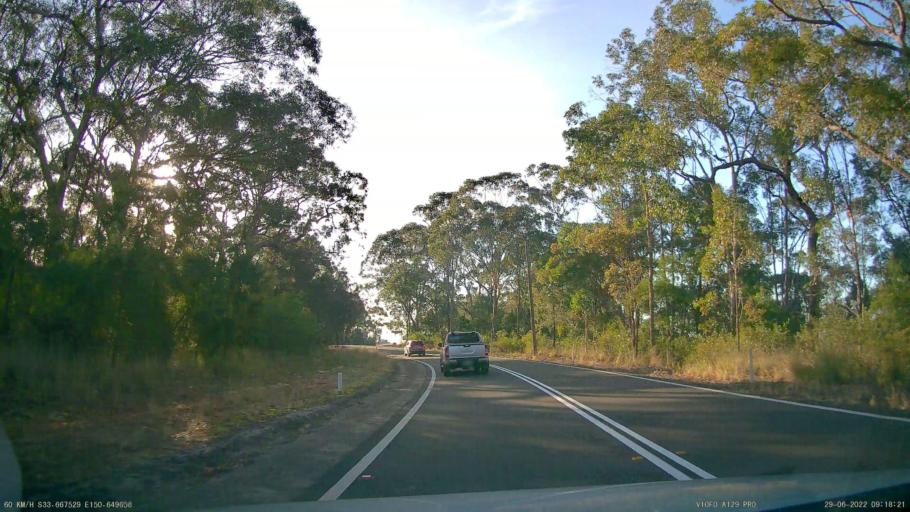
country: AU
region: New South Wales
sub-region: Penrith Municipality
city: Emu Heights
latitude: -33.6676
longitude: 150.6500
